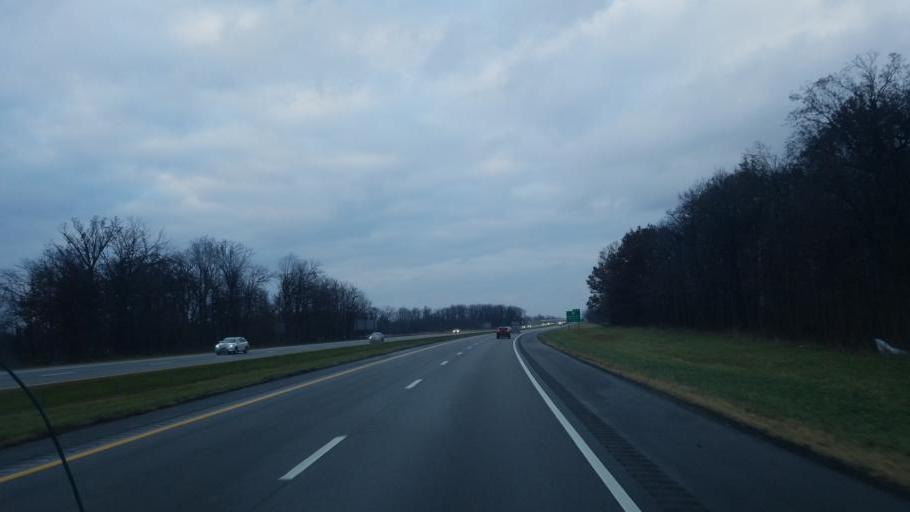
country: US
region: Ohio
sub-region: Auglaize County
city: Wapakoneta
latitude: 40.5753
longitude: -84.1695
